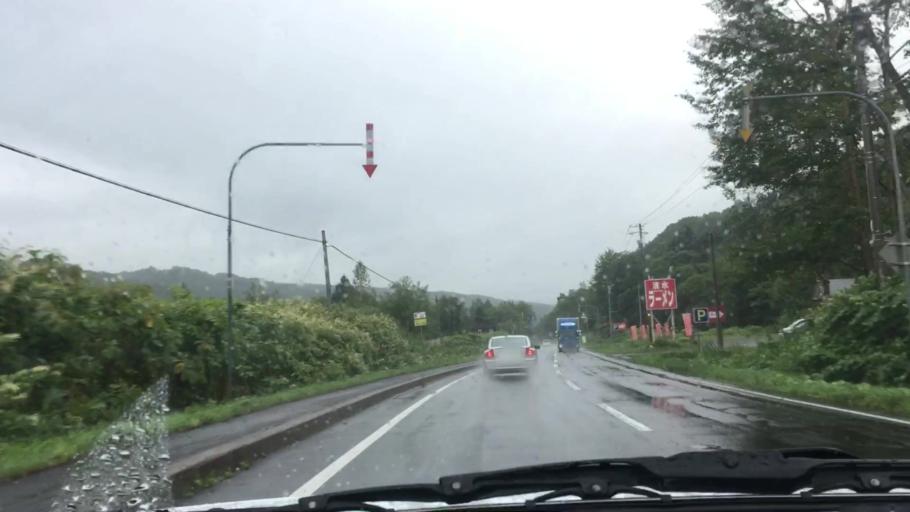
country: JP
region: Hokkaido
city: Niseko Town
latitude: 42.8084
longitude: 140.9999
